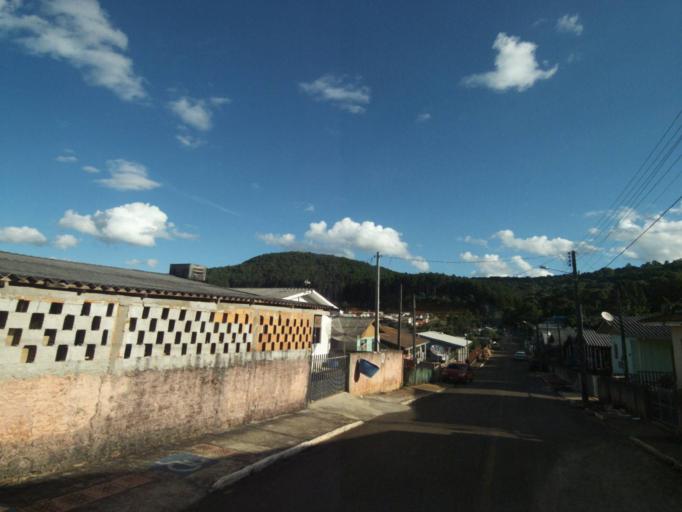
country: BR
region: Parana
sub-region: Uniao Da Vitoria
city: Uniao da Vitoria
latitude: -26.1664
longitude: -51.5372
